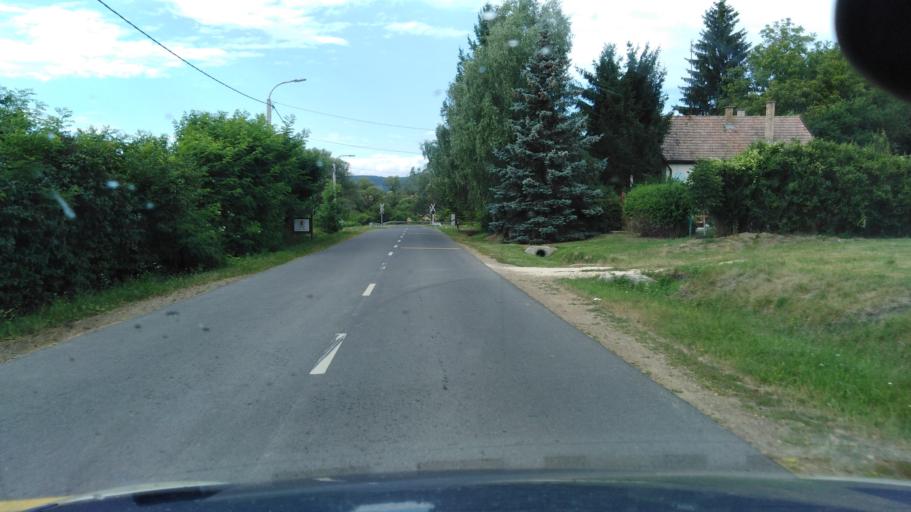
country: HU
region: Nograd
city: Szecseny
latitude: 48.1868
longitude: 19.5270
